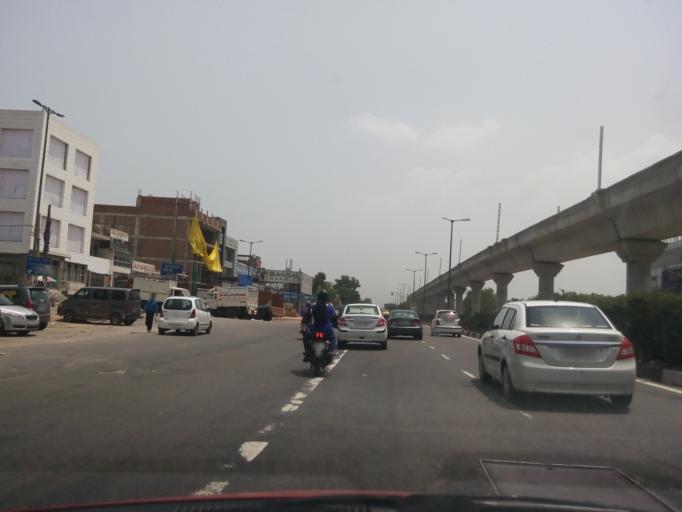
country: IN
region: NCT
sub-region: North West Delhi
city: Pitampura
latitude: 28.6454
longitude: 77.1270
